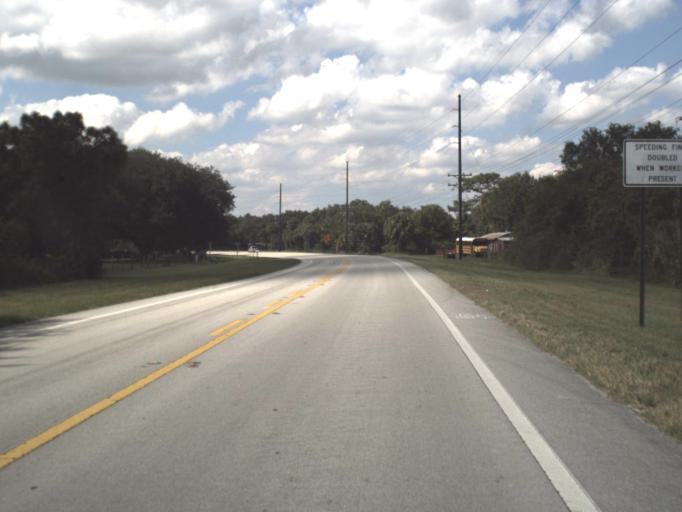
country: US
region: Florida
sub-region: Okeechobee County
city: Okeechobee
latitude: 27.3892
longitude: -81.0328
